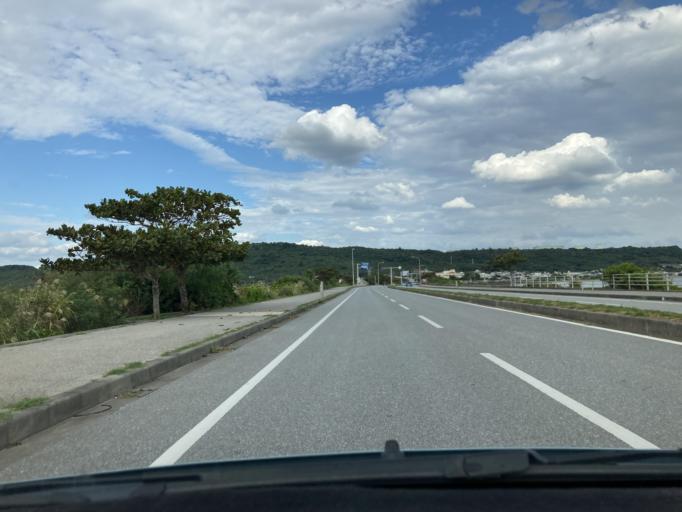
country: JP
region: Okinawa
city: Katsuren-haebaru
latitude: 26.3376
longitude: 127.9419
